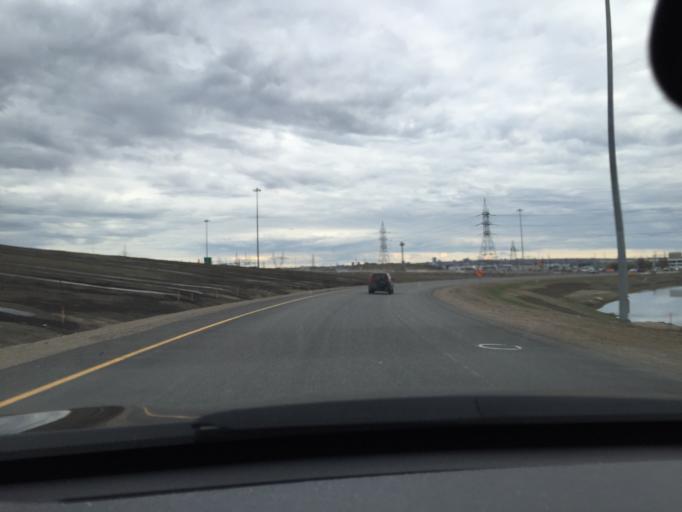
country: CA
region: Quebec
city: Quebec
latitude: 46.8380
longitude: -71.2663
